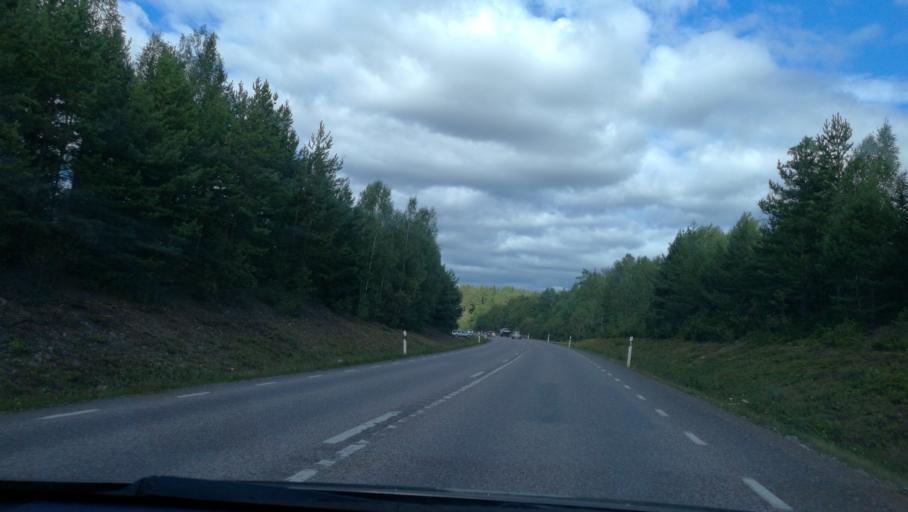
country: SE
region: Soedermanland
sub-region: Eskilstuna Kommun
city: Kvicksund
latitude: 59.5152
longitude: 16.3193
